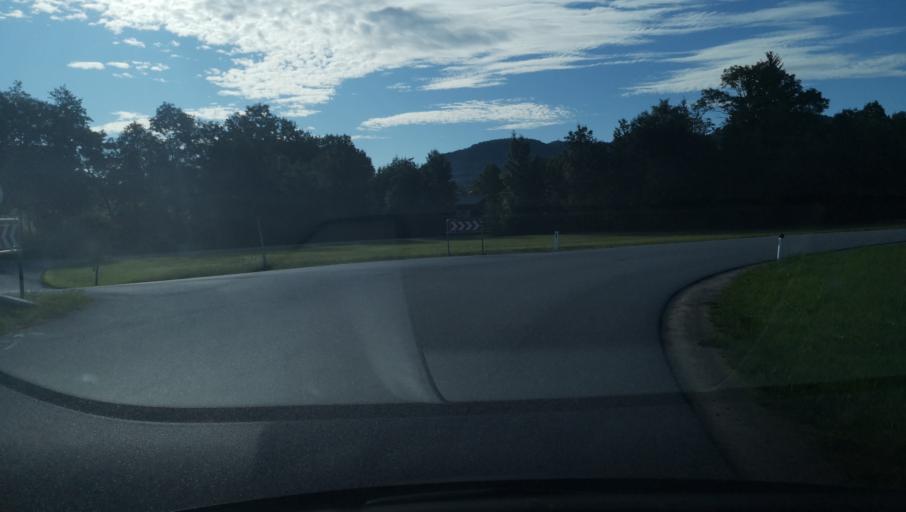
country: AT
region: Lower Austria
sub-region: Politischer Bezirk Scheibbs
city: Reinsberg
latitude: 48.0031
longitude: 15.0580
